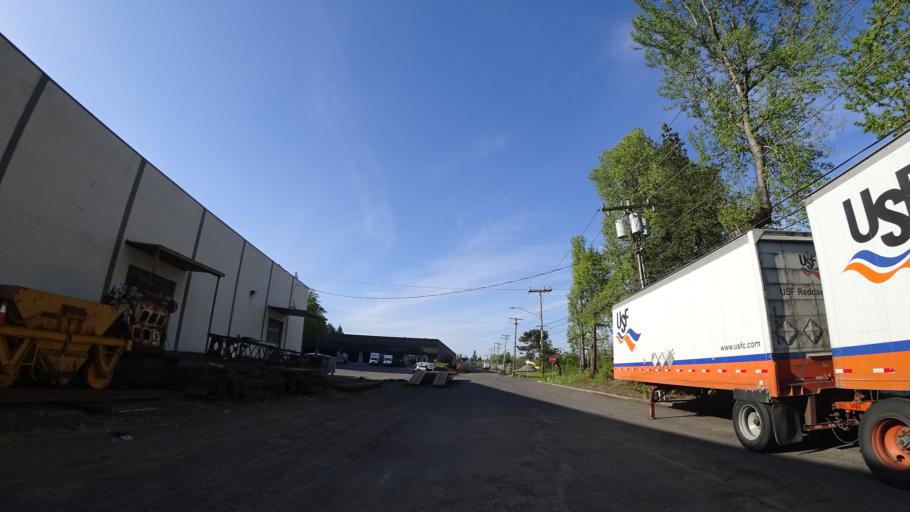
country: US
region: Oregon
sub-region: Clackamas County
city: Milwaukie
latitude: 45.4526
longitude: -122.6440
